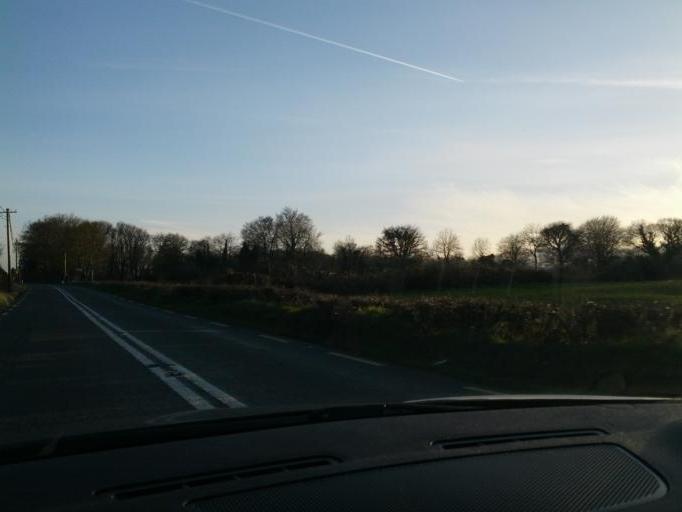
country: IE
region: Connaught
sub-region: Sligo
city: Tobercurry
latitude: 54.0788
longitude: -8.7032
